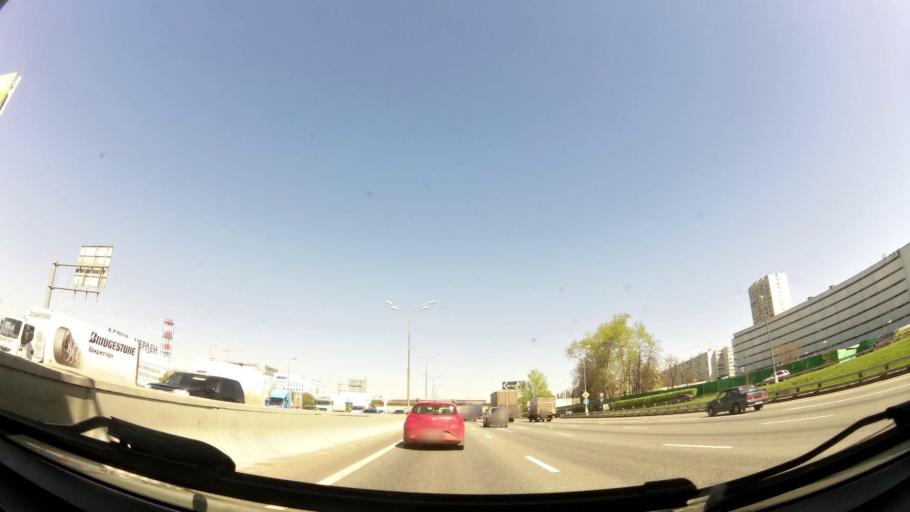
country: RU
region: Moscow
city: Strogino
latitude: 55.8093
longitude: 37.3886
